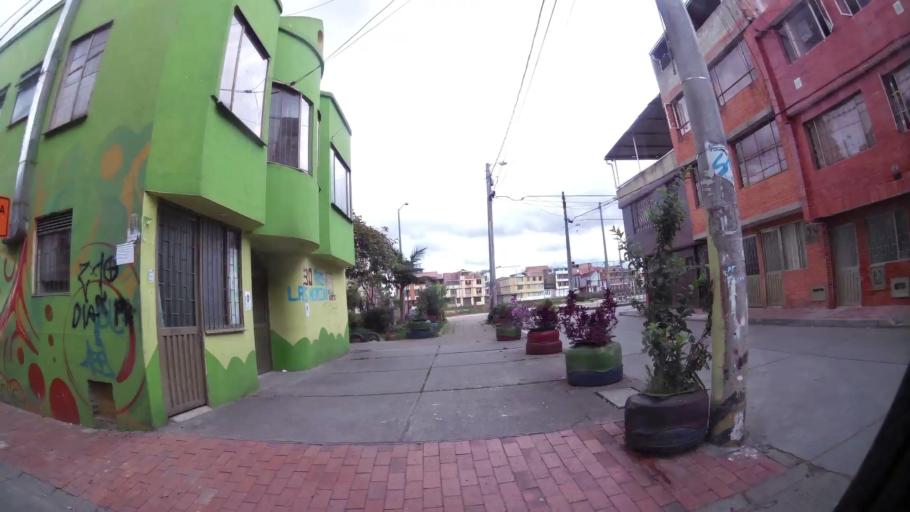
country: CO
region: Cundinamarca
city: Funza
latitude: 4.7024
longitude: -74.1275
